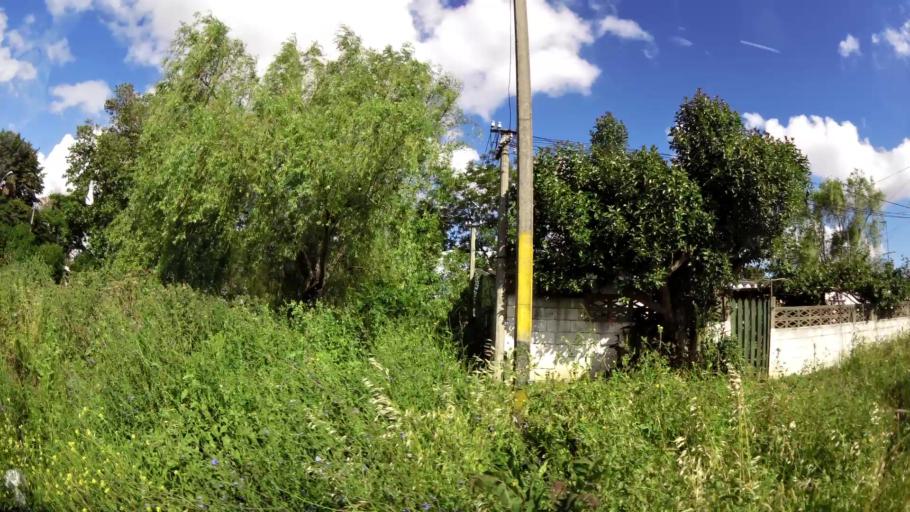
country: UY
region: Canelones
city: La Paz
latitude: -34.8121
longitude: -56.2266
